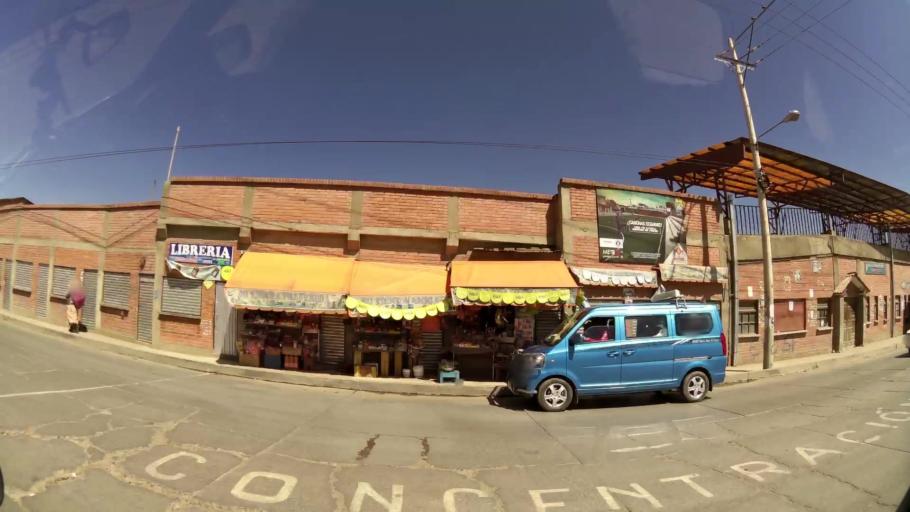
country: BO
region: La Paz
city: La Paz
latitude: -16.5452
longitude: -68.1962
